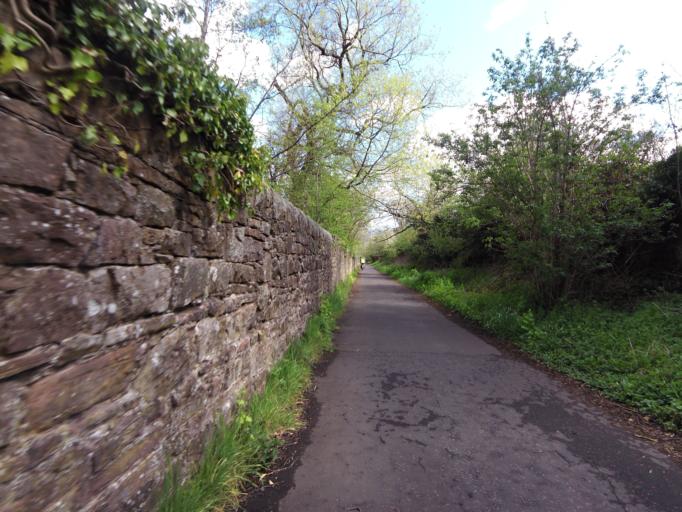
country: GB
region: Scotland
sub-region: West Lothian
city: Seafield
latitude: 55.9383
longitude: -3.1553
